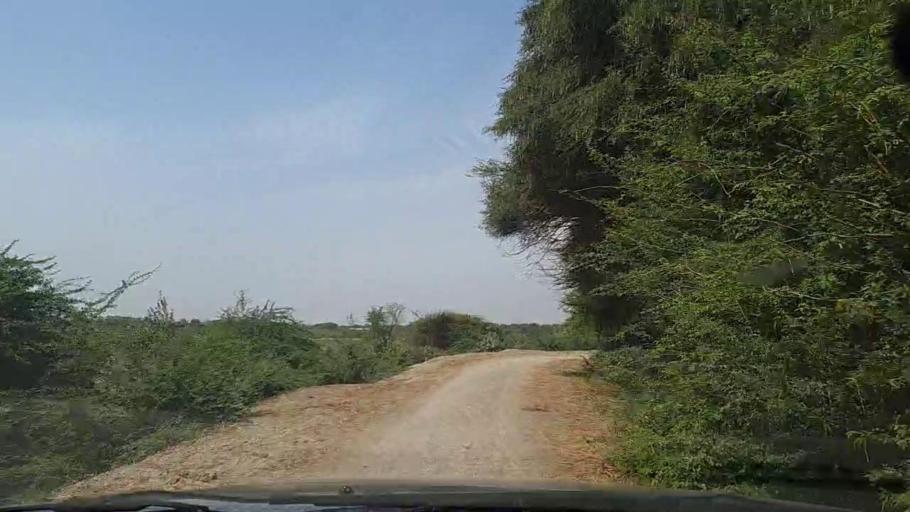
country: PK
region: Sindh
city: Mirpur Batoro
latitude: 24.6525
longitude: 68.1682
